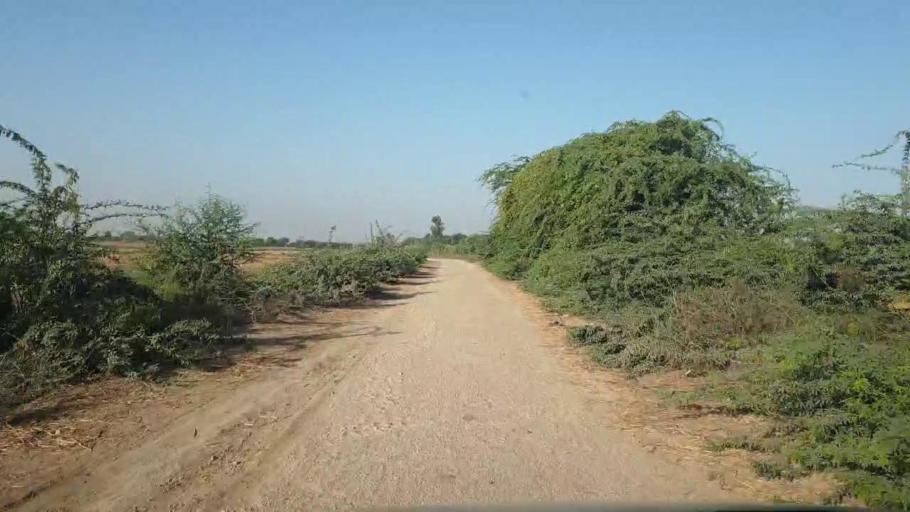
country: PK
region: Sindh
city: Badin
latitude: 24.6876
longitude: 68.8210
